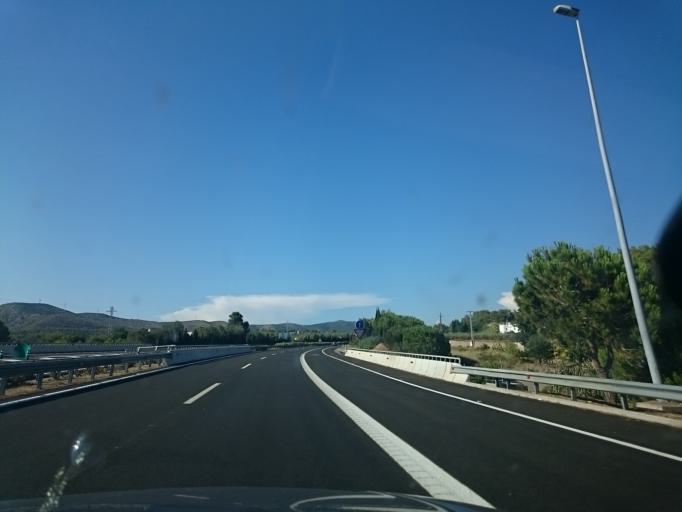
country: ES
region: Catalonia
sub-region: Provincia de Barcelona
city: Cubelles
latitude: 41.2279
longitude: 1.6777
